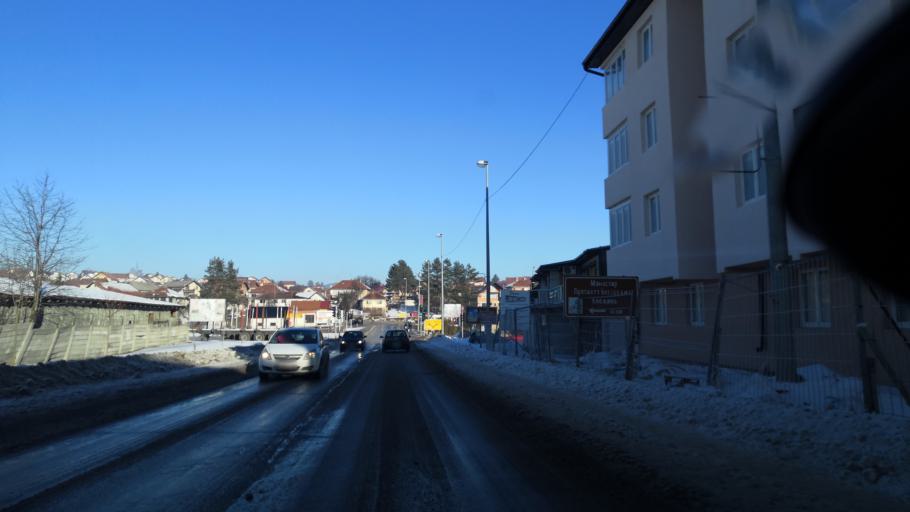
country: BA
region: Republika Srpska
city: Sokolac
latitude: 43.9376
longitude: 18.7967
